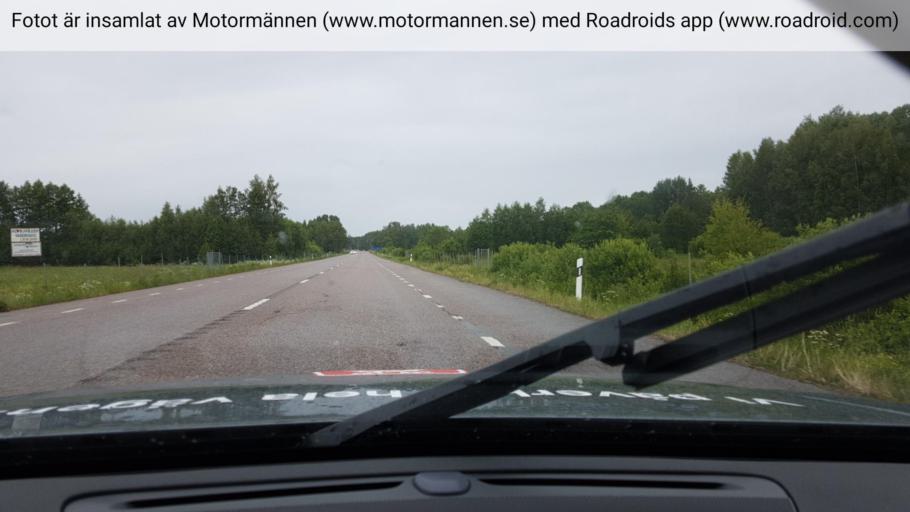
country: SE
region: Uppsala
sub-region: Alvkarleby Kommun
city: AElvkarleby
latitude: 60.5783
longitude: 17.4659
